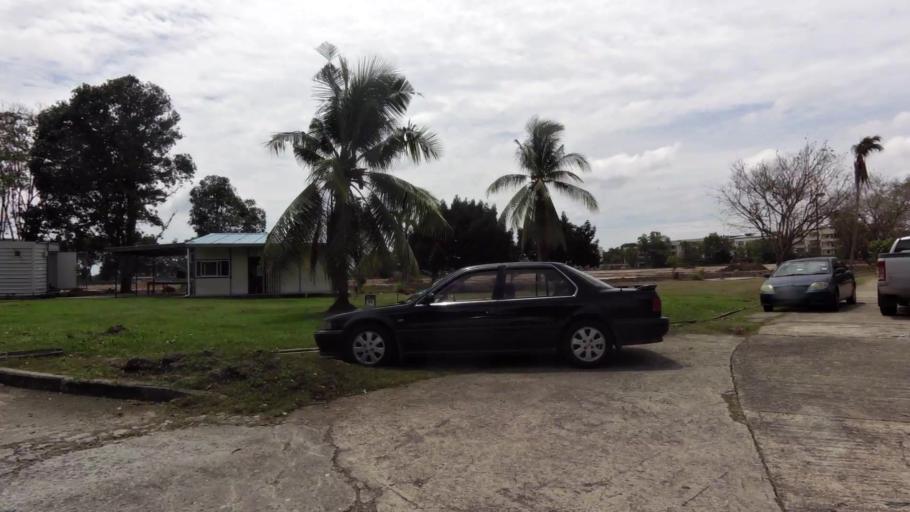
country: BN
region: Brunei and Muara
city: Bandar Seri Begawan
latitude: 4.9306
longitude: 114.9428
